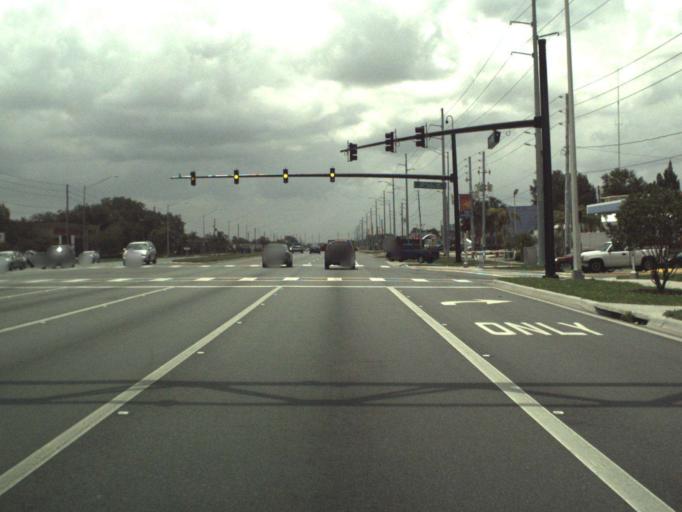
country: US
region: Florida
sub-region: Seminole County
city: Fern Park
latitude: 28.6512
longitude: -81.3278
